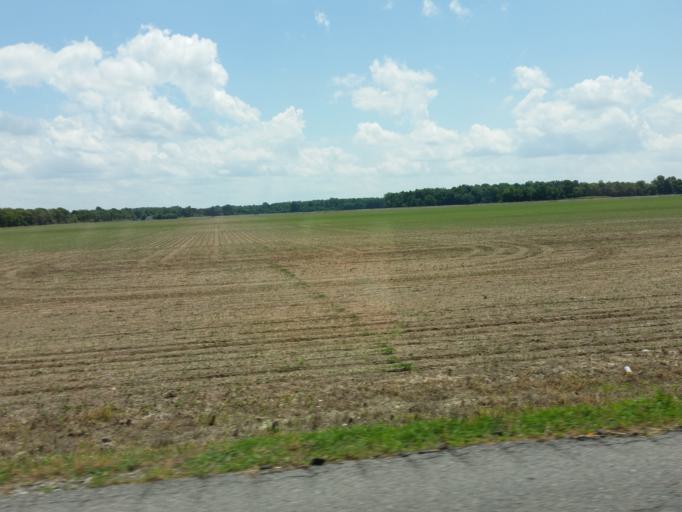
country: US
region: Kentucky
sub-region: Fulton County
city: Hickman
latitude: 36.5235
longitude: -89.3387
